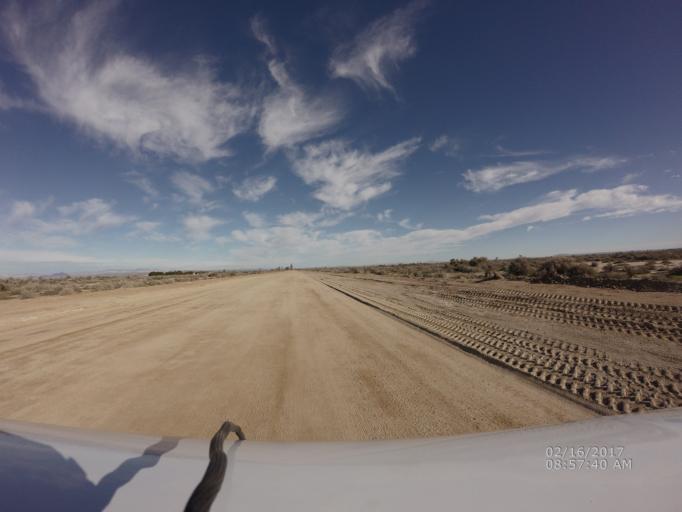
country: US
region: California
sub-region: Kern County
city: Edwards Air Force Base
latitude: 34.7641
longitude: -117.9521
